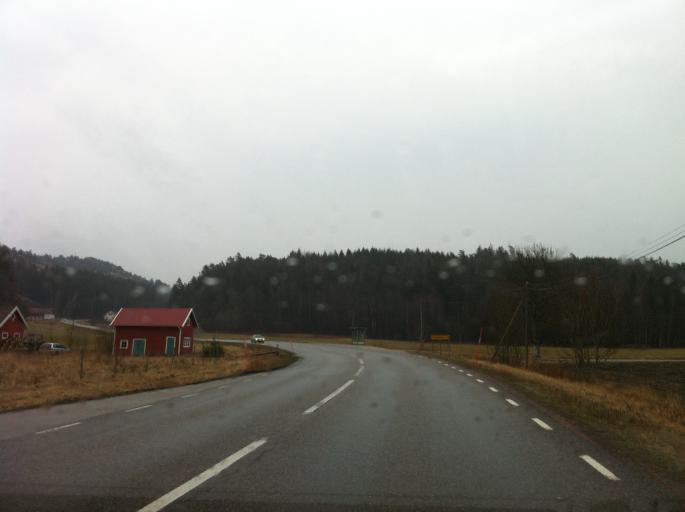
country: SE
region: Vaestra Goetaland
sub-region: Lysekils Kommun
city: Brastad
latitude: 58.4547
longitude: 11.4718
